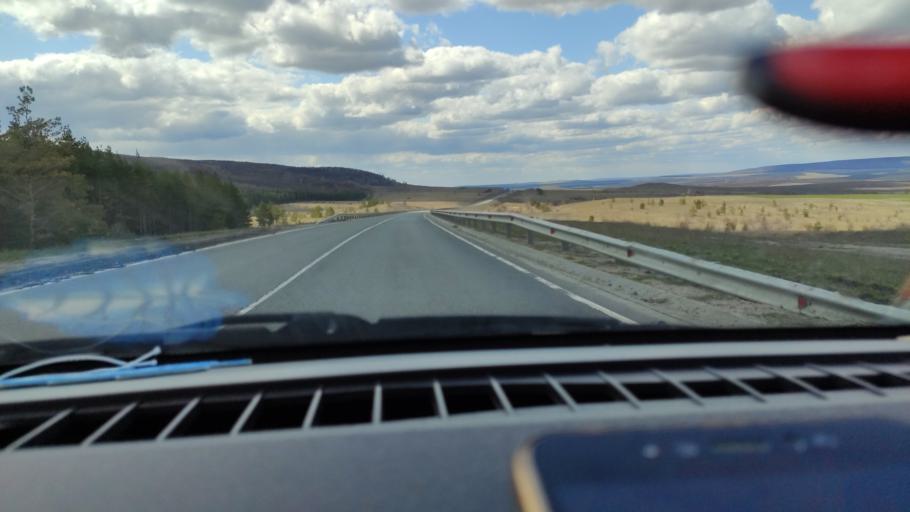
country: RU
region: Saratov
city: Alekseyevka
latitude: 52.3655
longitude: 47.9609
